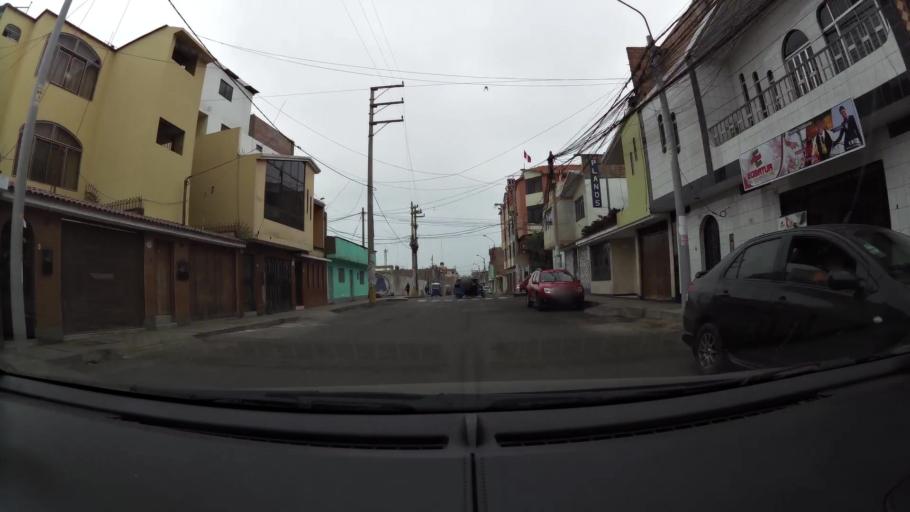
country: PE
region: Lima
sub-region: Barranca
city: Barranca
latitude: -10.7576
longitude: -77.7585
